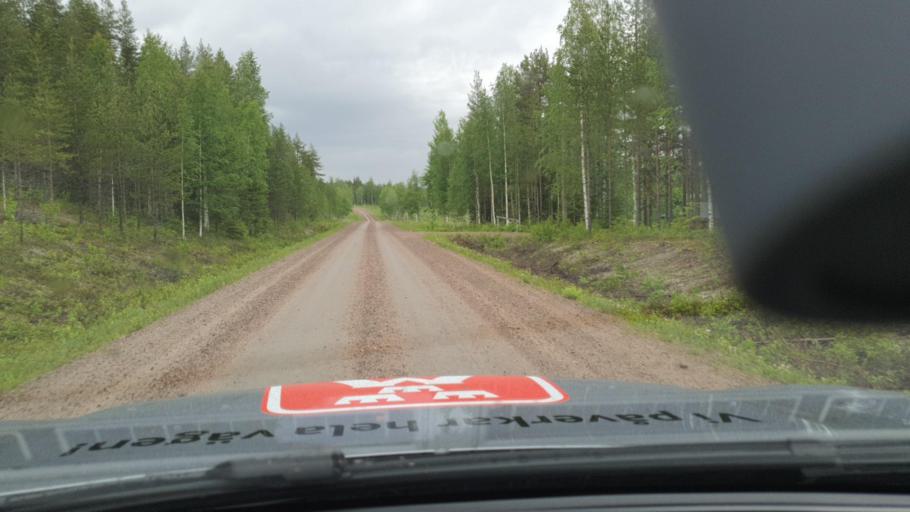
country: SE
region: Norrbotten
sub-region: Overkalix Kommun
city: OEverkalix
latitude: 66.6030
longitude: 22.7478
